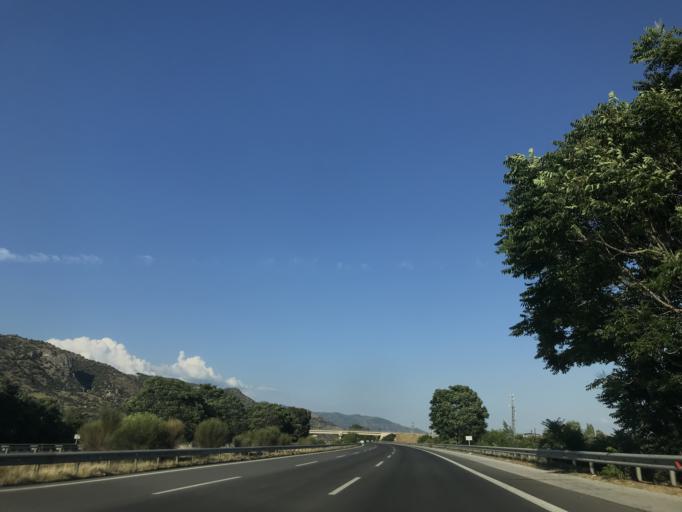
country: TR
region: Aydin
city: Incirliova
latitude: 37.8681
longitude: 27.7241
